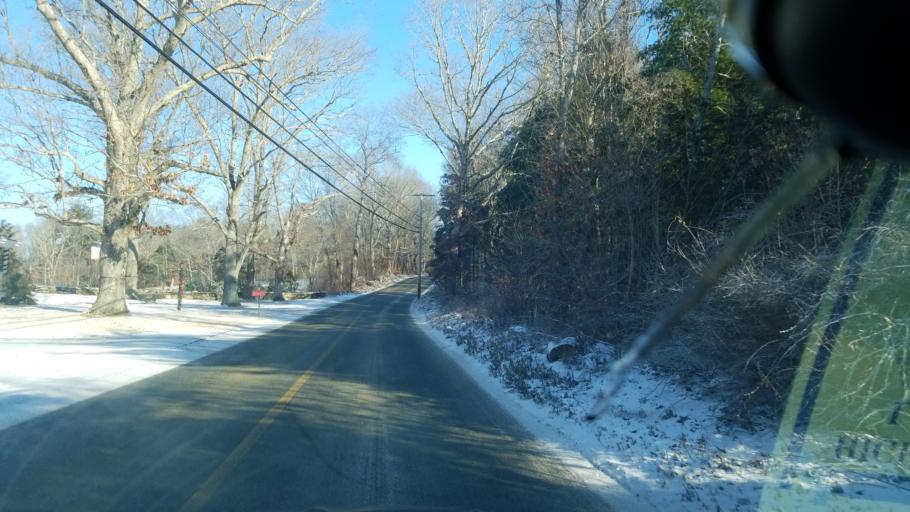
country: US
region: Connecticut
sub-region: Windham County
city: East Brooklyn
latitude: 41.7888
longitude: -71.9184
